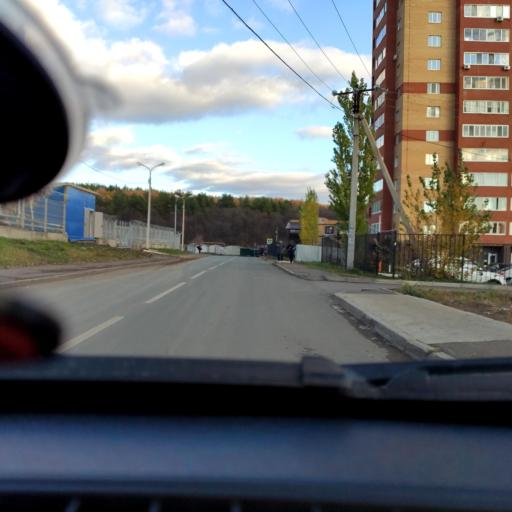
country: RU
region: Bashkortostan
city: Ufa
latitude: 54.6910
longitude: 55.9971
